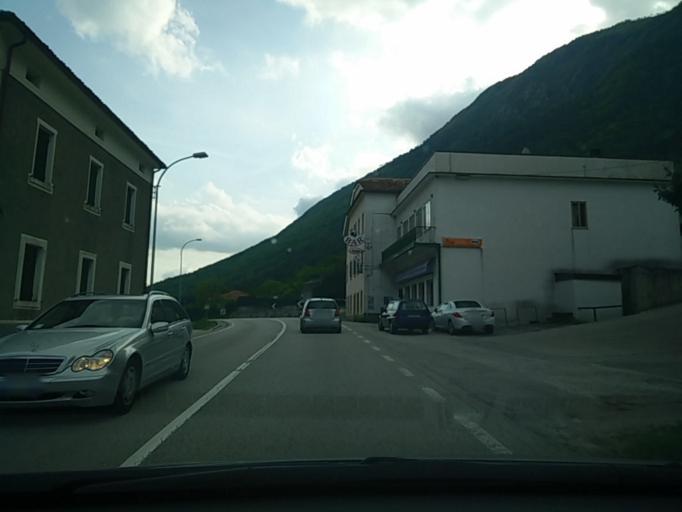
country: IT
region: Veneto
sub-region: Provincia di Treviso
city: Fregona
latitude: 46.0472
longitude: 12.3096
